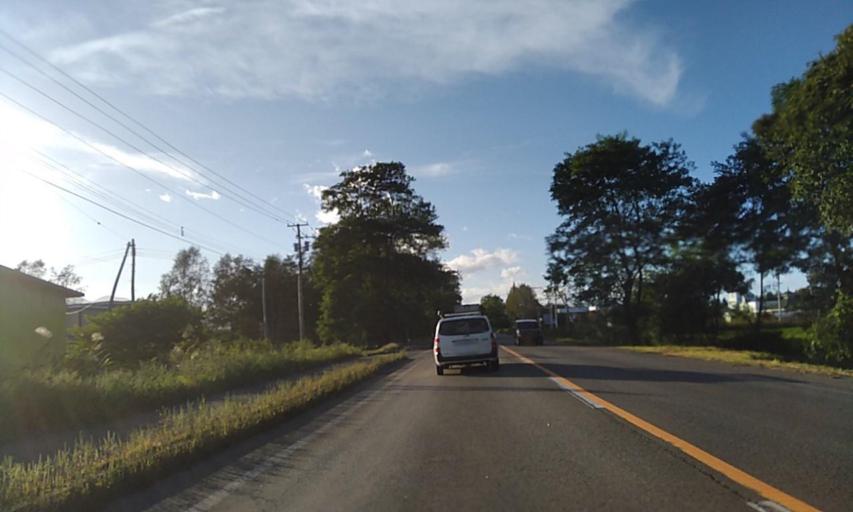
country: JP
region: Hokkaido
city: Obihiro
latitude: 42.9372
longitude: 142.9625
